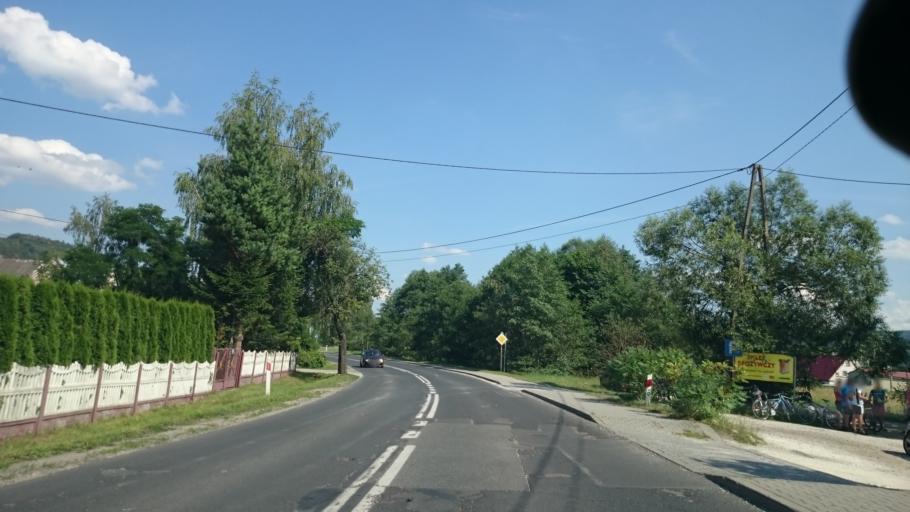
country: PL
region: Lower Silesian Voivodeship
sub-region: Powiat klodzki
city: Bystrzyca Klodzka
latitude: 50.3551
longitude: 16.7305
